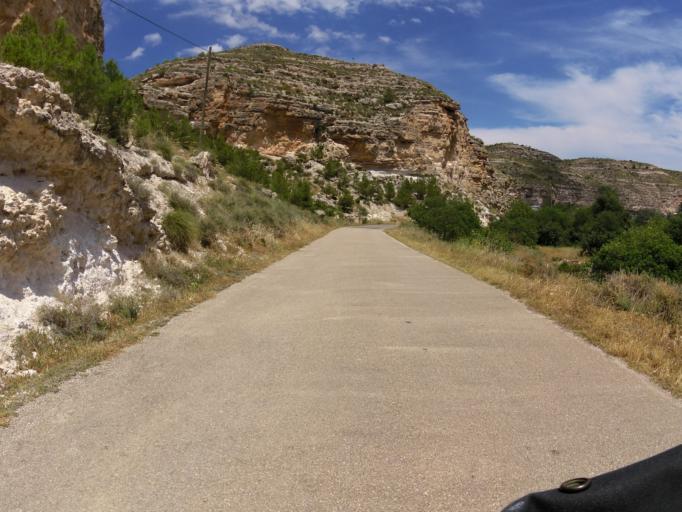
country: ES
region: Castille-La Mancha
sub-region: Provincia de Albacete
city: Jorquera
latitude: 39.1683
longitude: -1.5602
